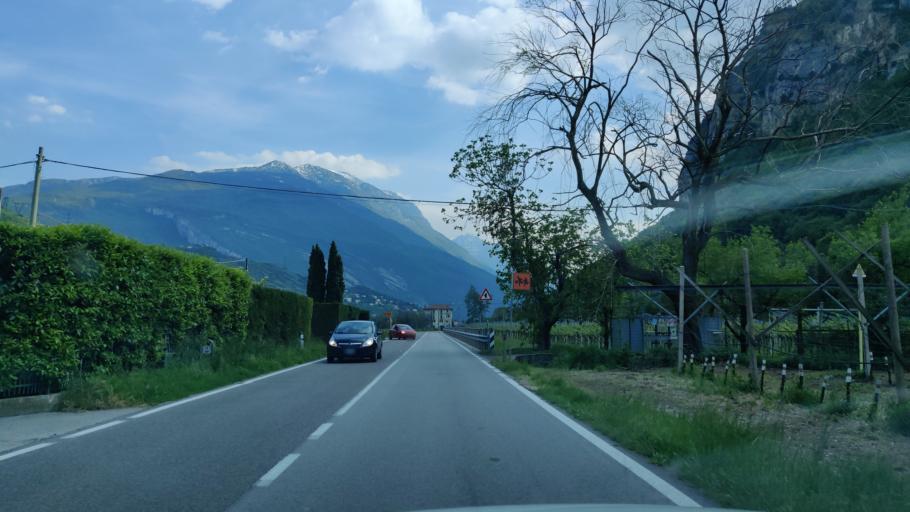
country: IT
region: Trentino-Alto Adige
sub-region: Provincia di Trento
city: Nago-Torbole
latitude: 45.8910
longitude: 10.8793
